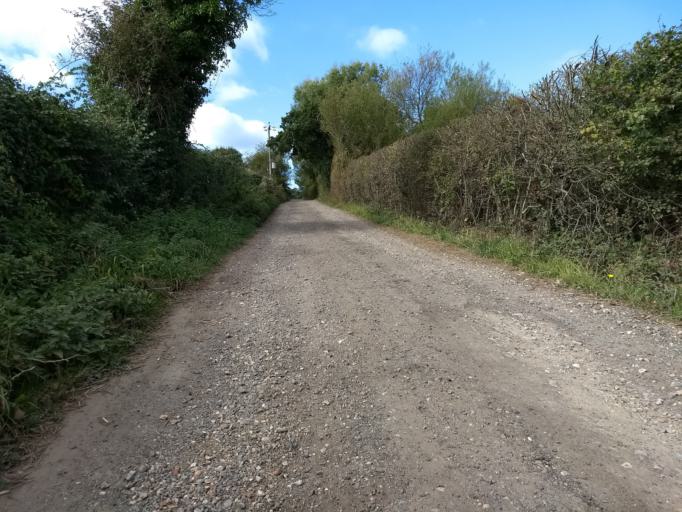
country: GB
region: England
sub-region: Isle of Wight
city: Seaview
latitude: 50.7117
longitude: -1.1311
